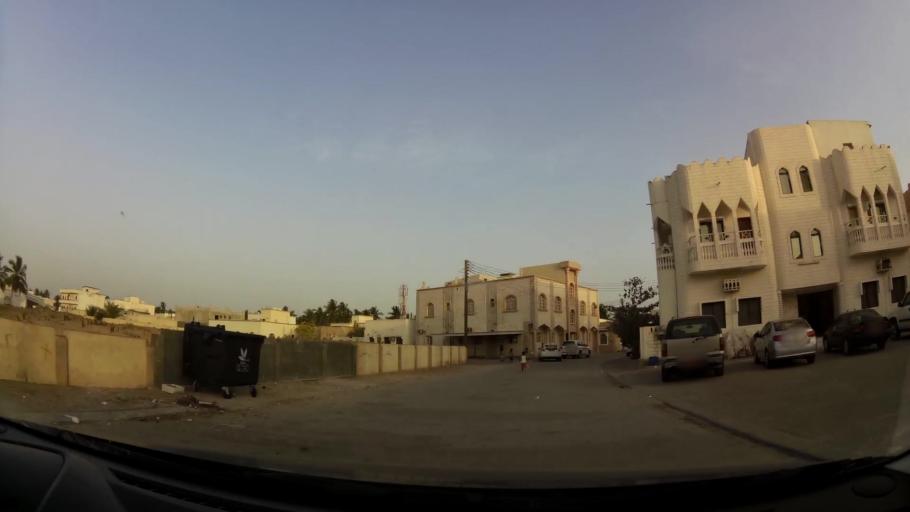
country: OM
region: Zufar
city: Salalah
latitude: 17.0184
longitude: 54.1151
